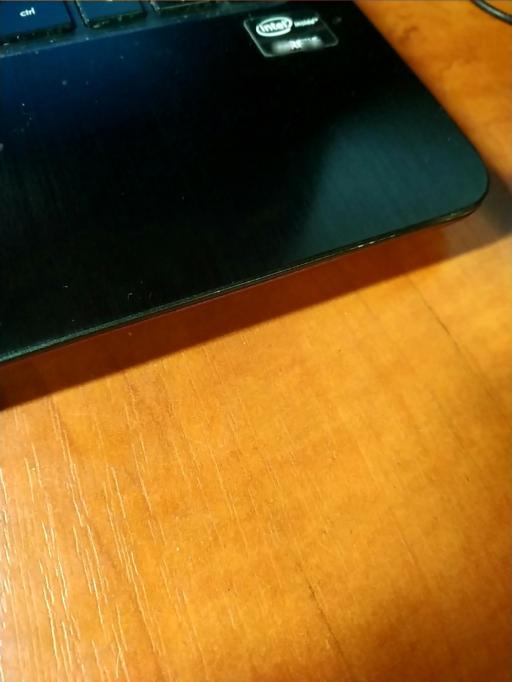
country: RU
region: Tverskaya
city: Zubtsov
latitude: 56.2390
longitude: 34.7044
